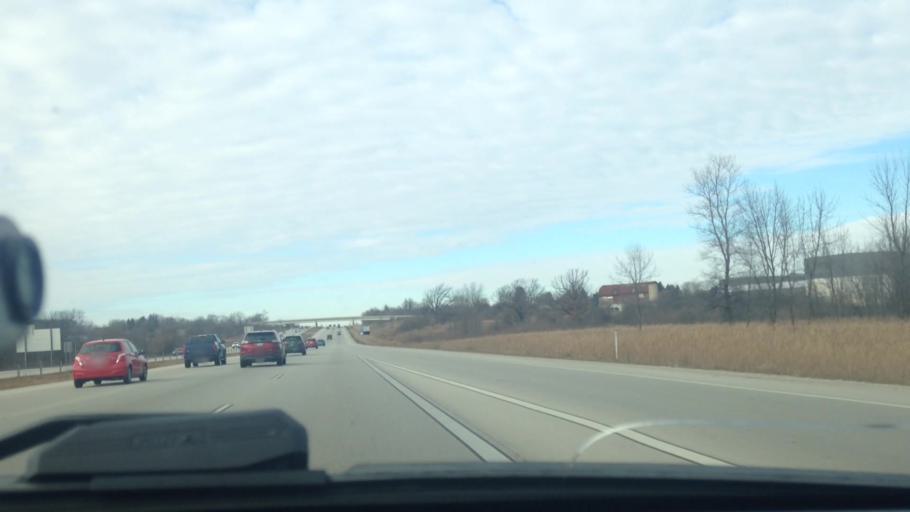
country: US
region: Wisconsin
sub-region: Washington County
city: Germantown
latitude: 43.2162
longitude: -88.1506
